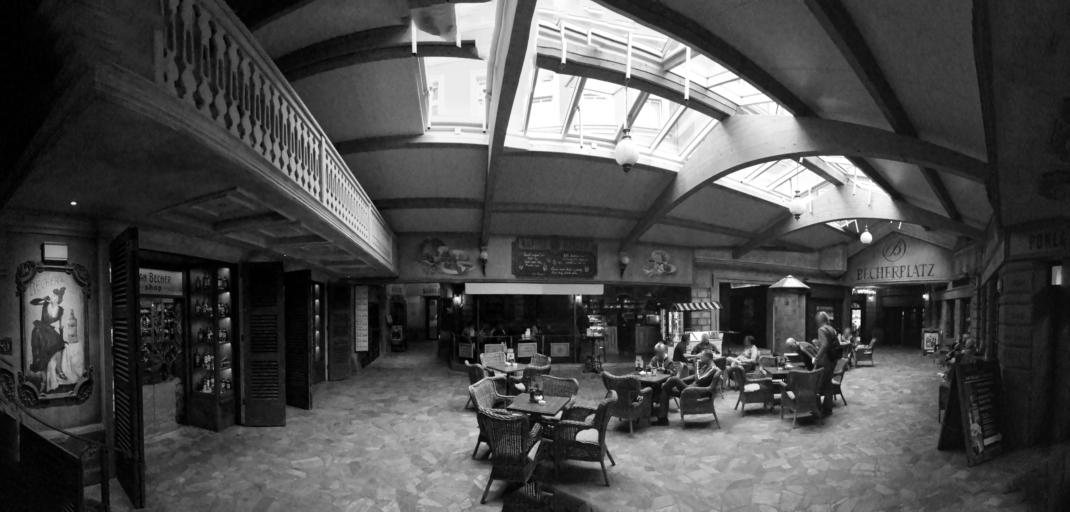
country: CZ
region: Karlovarsky
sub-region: Okres Karlovy Vary
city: Karlovy Vary
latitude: 50.2303
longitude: 12.8673
